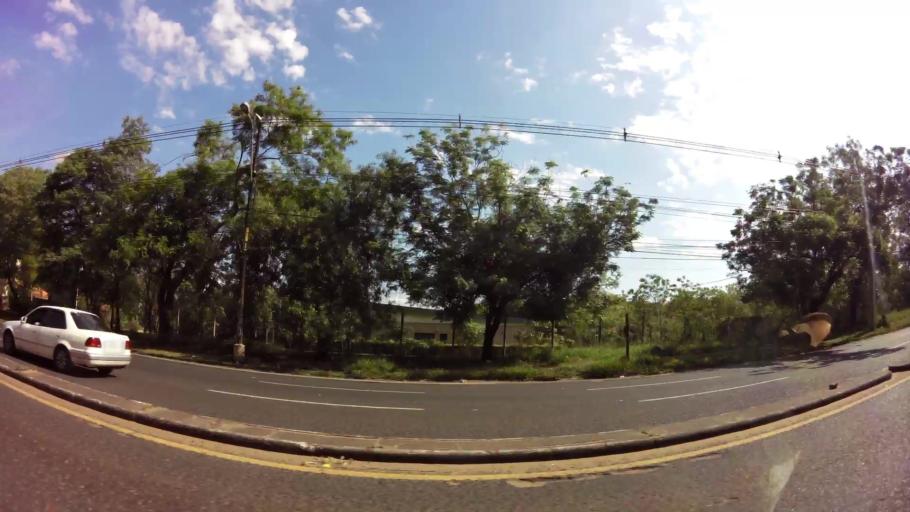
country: PY
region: Central
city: Fernando de la Mora
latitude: -25.3379
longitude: -57.5261
